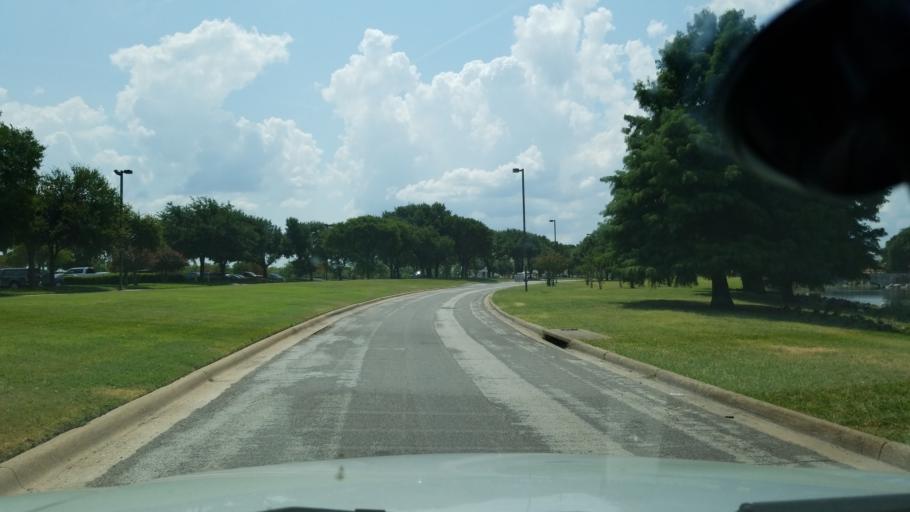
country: US
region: Texas
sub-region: Dallas County
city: Farmers Branch
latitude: 32.8610
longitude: -96.8953
